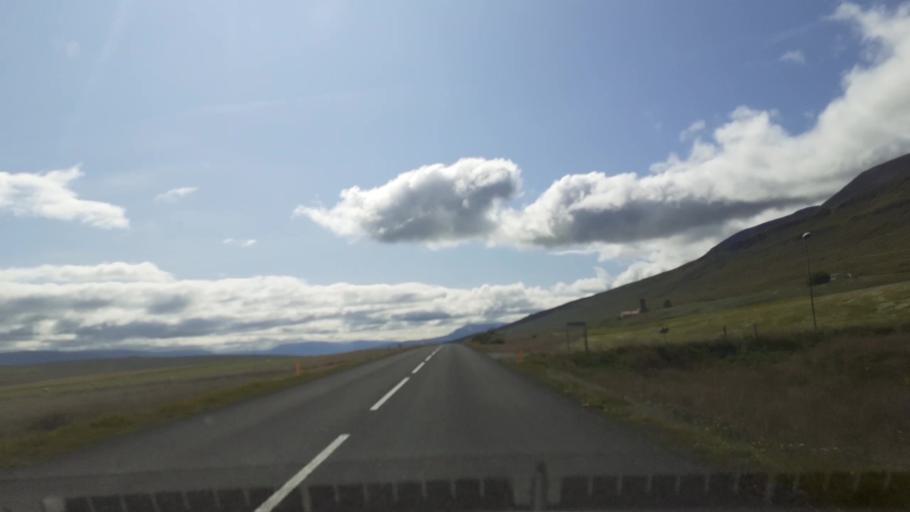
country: IS
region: Northeast
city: Akureyri
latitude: 65.8625
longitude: -18.2609
